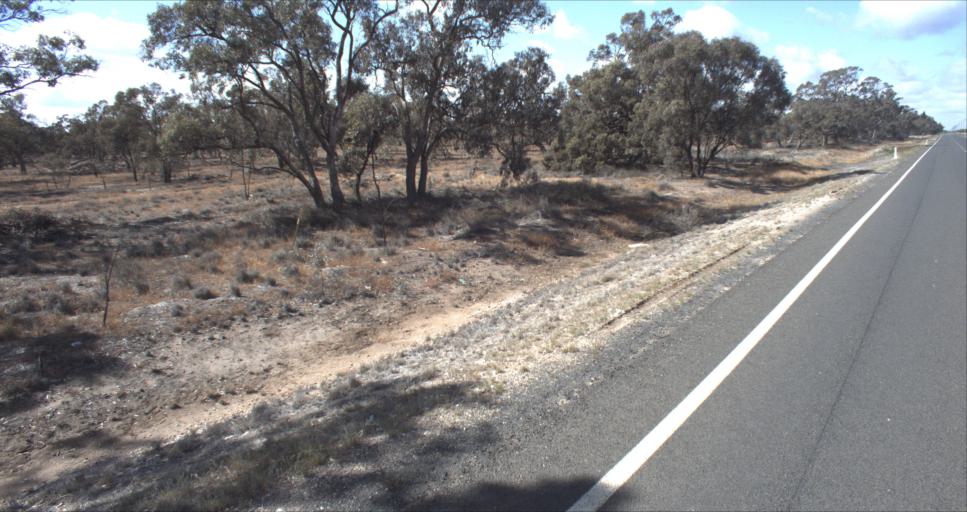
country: AU
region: New South Wales
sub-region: Murrumbidgee Shire
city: Darlington Point
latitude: -34.5228
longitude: 146.1754
